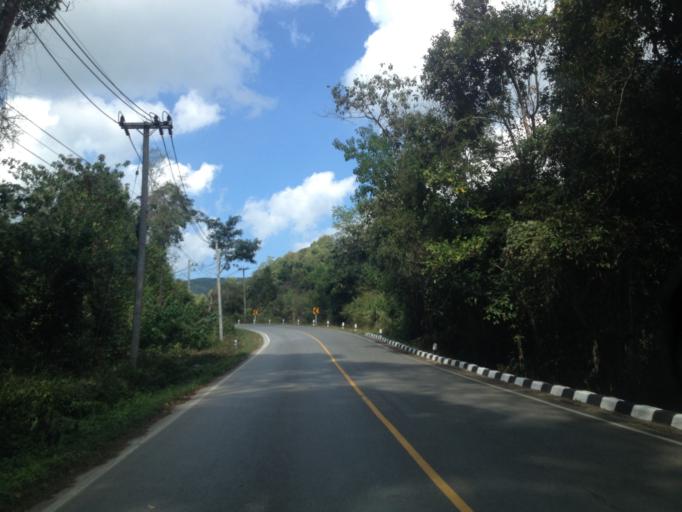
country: TH
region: Mae Hong Son
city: Ban Huai I Huak
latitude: 18.1495
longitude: 98.1422
